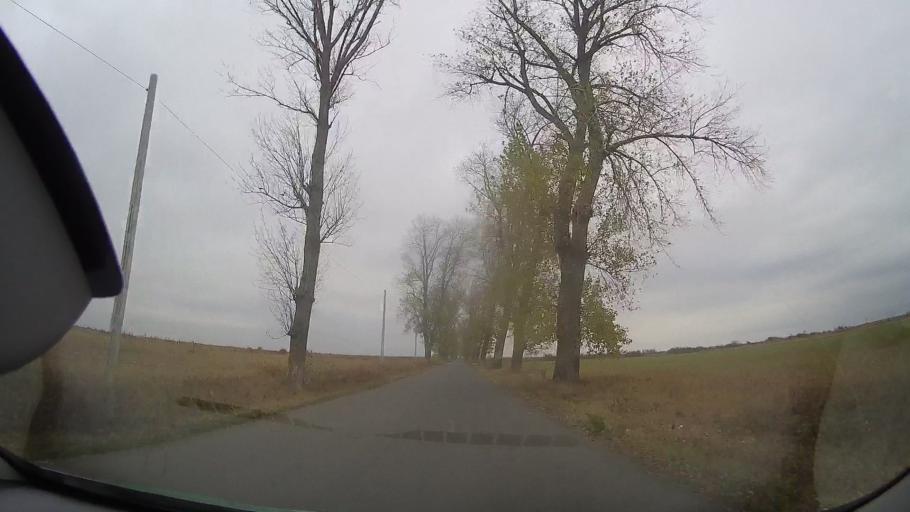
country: RO
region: Braila
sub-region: Comuna Ciocile
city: Ciocile
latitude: 44.8123
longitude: 27.2849
